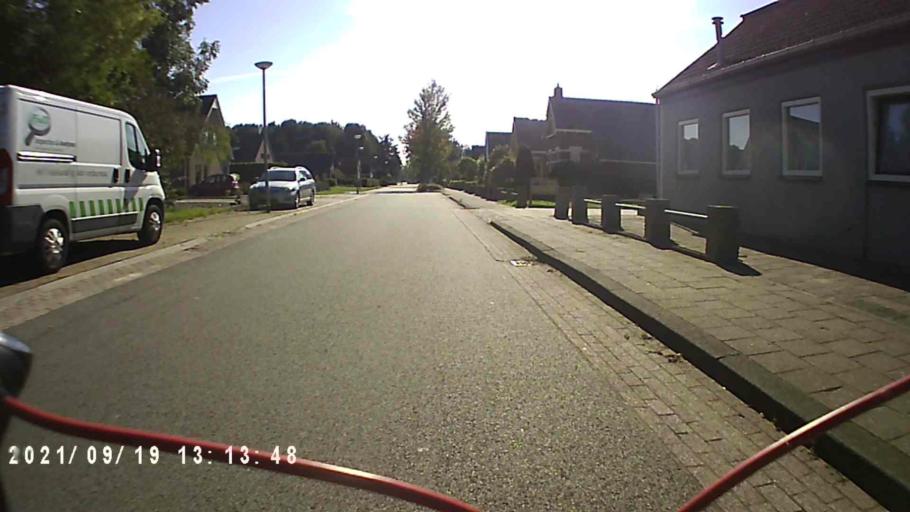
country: NL
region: Groningen
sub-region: Gemeente  Oldambt
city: Winschoten
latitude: 53.1623
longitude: 6.9867
